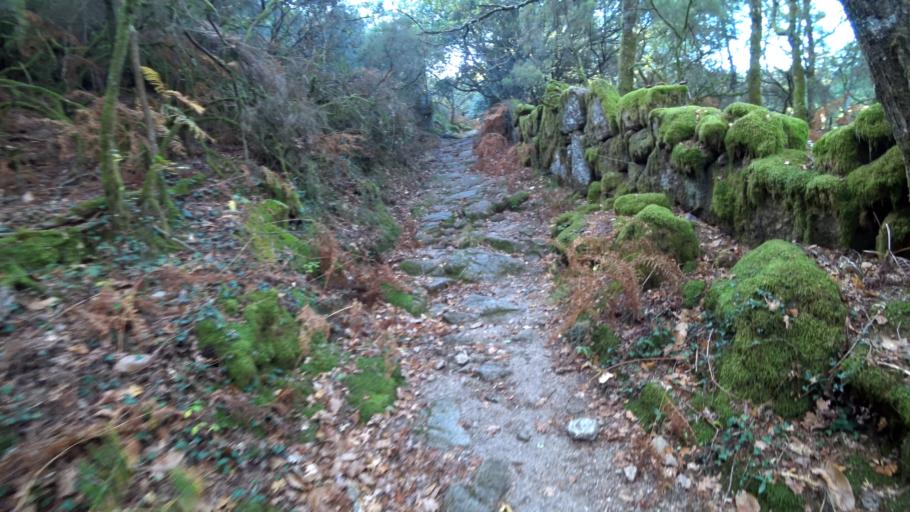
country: PT
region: Braga
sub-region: Terras de Bouro
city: Antas
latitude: 41.7710
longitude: -8.1841
